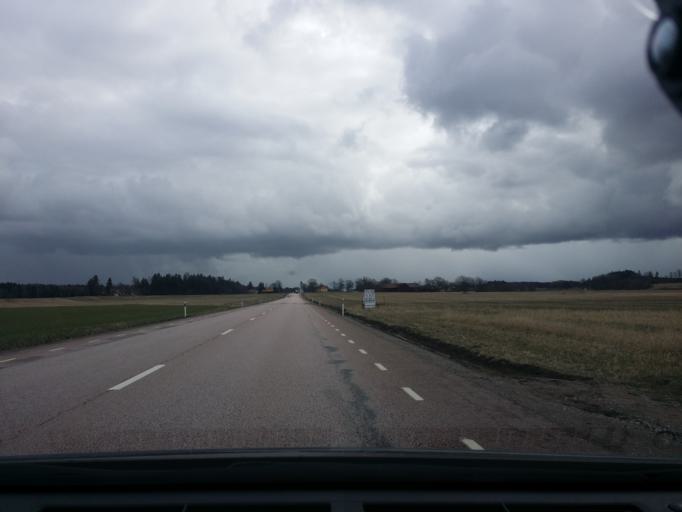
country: SE
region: Uppsala
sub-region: Enkopings Kommun
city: Irsta
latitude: 59.7763
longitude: 16.8709
